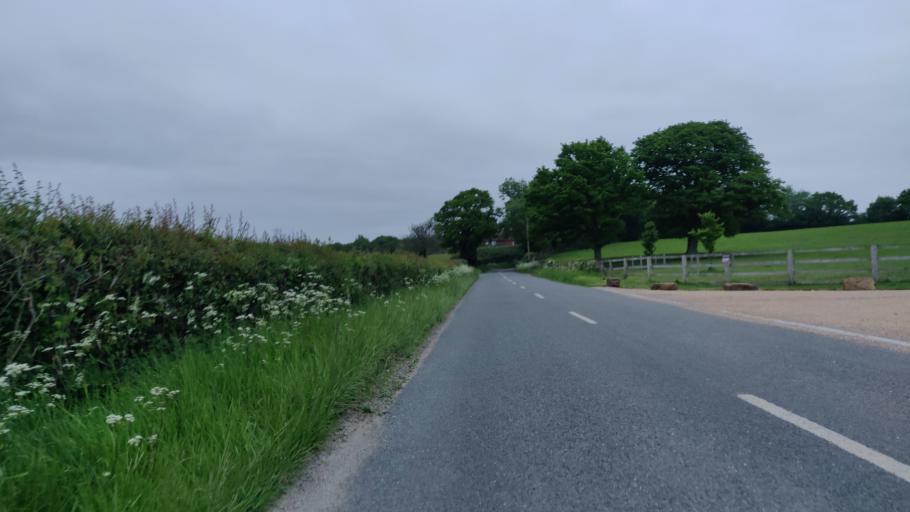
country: GB
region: England
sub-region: West Sussex
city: Partridge Green
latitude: 50.9777
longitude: -0.3017
